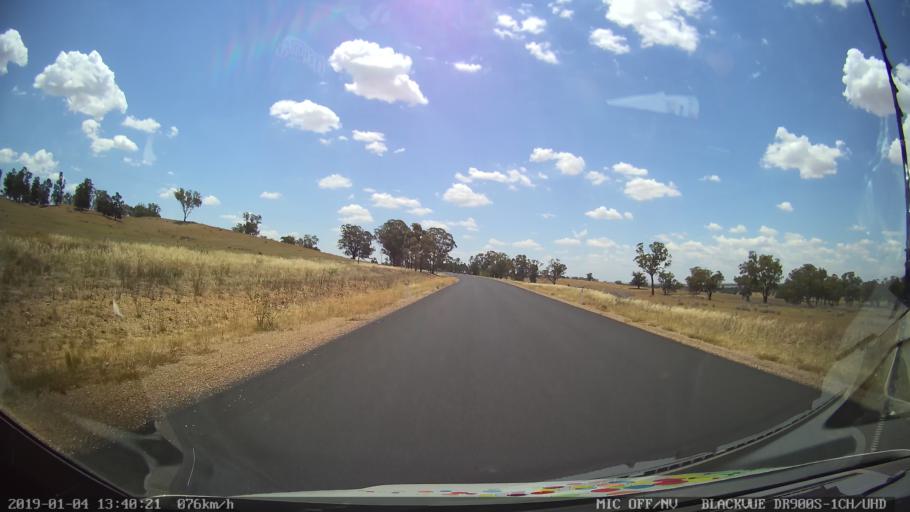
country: AU
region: New South Wales
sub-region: Dubbo Municipality
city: Dubbo
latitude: -32.5152
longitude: 148.5552
